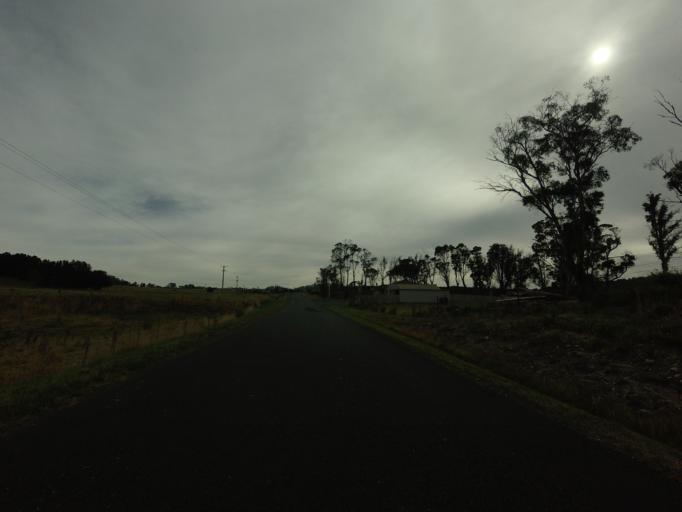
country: AU
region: Tasmania
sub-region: Sorell
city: Sorell
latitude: -42.4585
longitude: 147.5733
